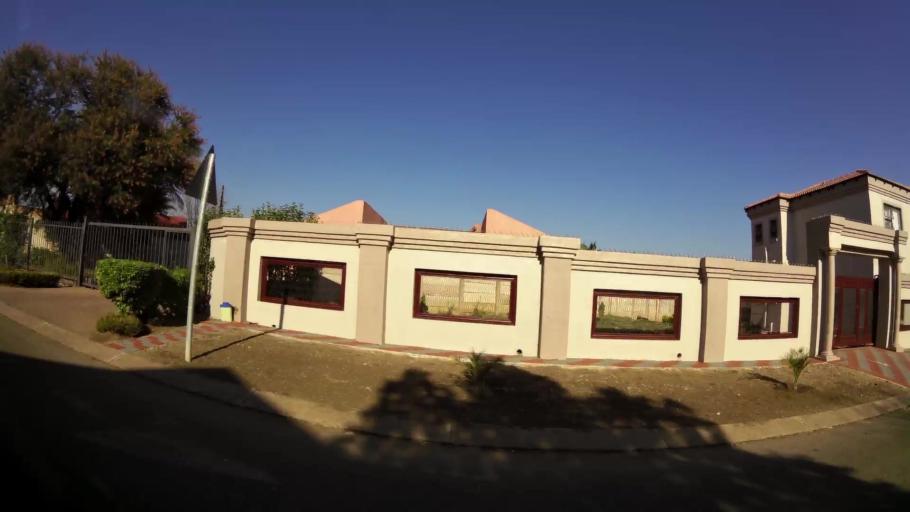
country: ZA
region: Gauteng
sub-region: City of Tshwane Metropolitan Municipality
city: Pretoria
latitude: -25.6708
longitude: 28.2214
